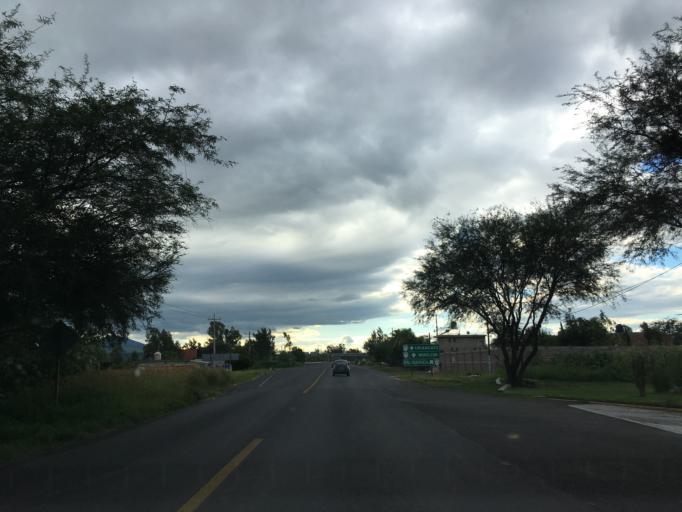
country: MX
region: Michoacan
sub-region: Cuitzeo
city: Cuamio
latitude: 20.0756
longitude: -101.1314
